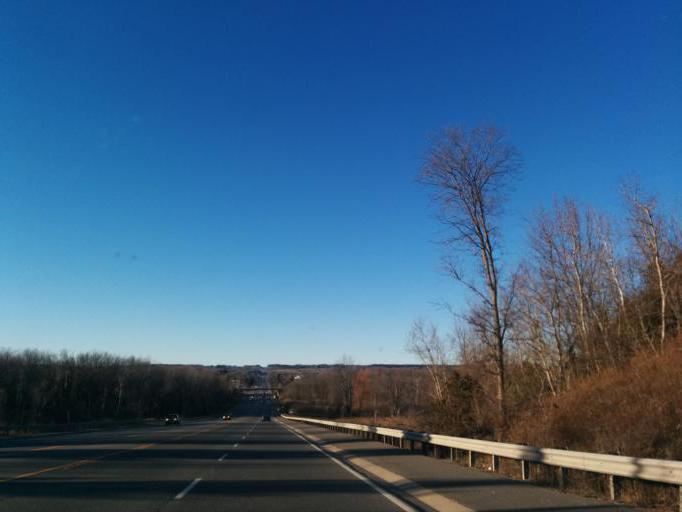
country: CA
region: Ontario
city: Brampton
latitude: 43.8081
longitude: -79.9255
